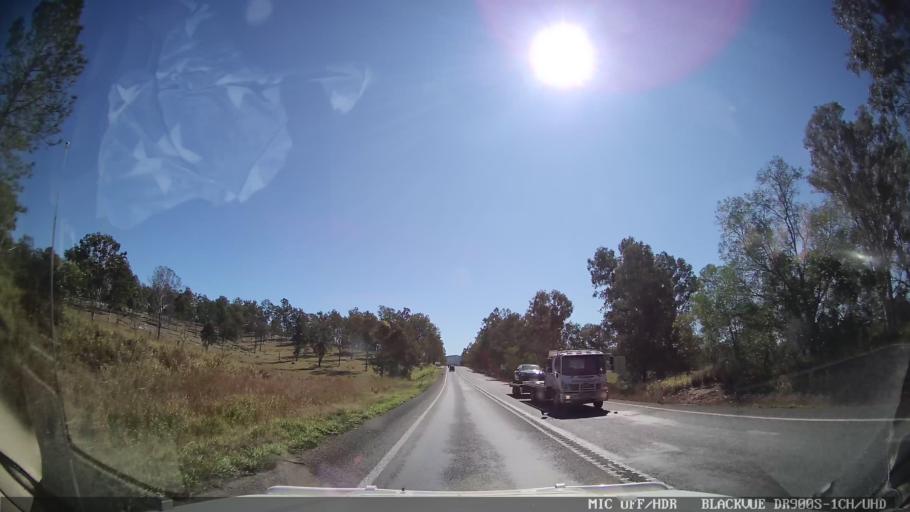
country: AU
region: Queensland
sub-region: Gympie Regional Council
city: Gympie
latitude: -26.0033
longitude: 152.5666
